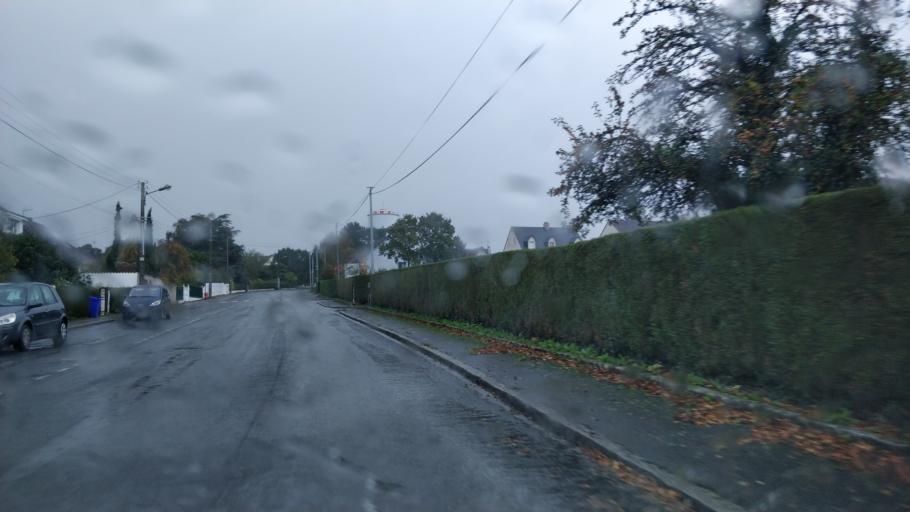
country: FR
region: Lower Normandy
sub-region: Departement de la Manche
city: Brehal
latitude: 48.9010
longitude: -1.5193
